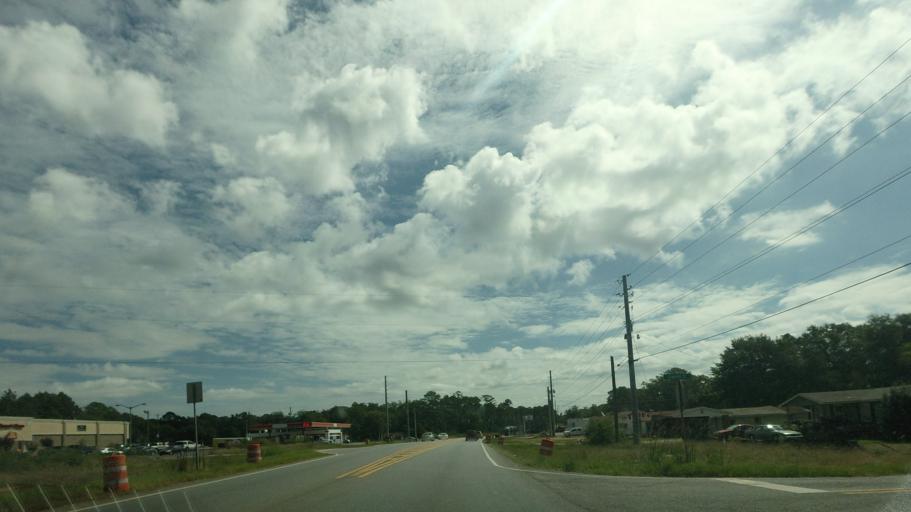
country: US
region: Georgia
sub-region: Houston County
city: Robins Air Force Base
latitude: 32.5544
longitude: -83.6262
